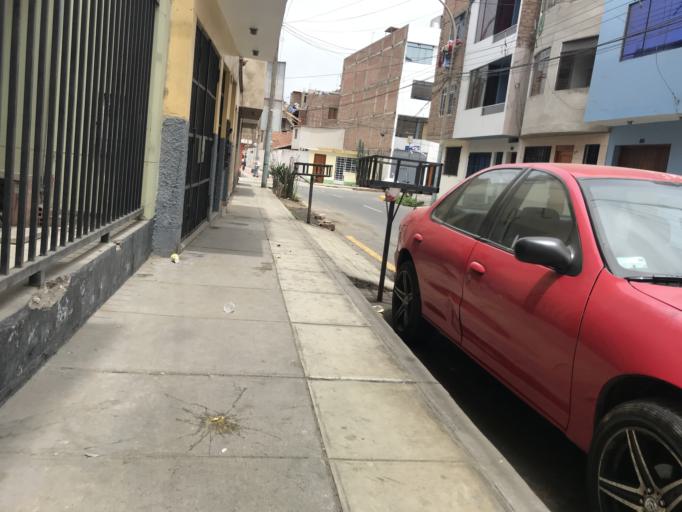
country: PE
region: Lima
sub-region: Lima
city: San Isidro
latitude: -12.0838
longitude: -77.0752
